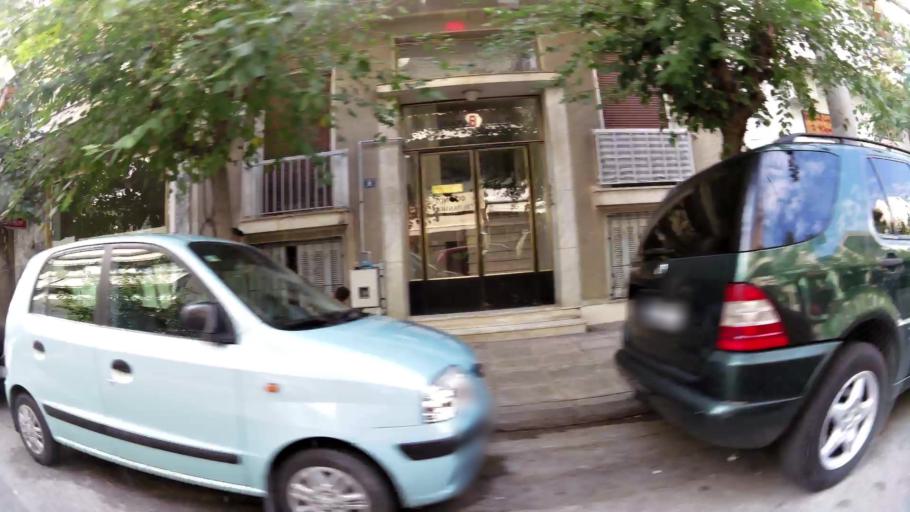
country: GR
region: Attica
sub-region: Nomarchia Athinas
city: Nea Smyrni
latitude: 37.9551
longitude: 23.7168
